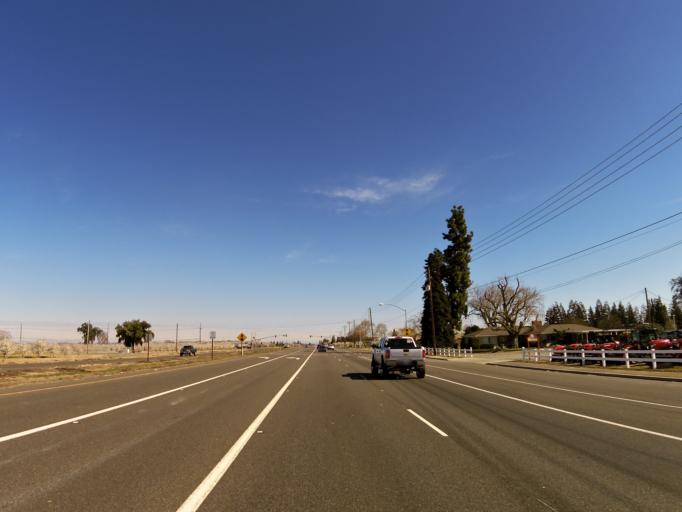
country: US
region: California
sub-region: Stanislaus County
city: Salida
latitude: 37.7110
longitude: -121.0720
